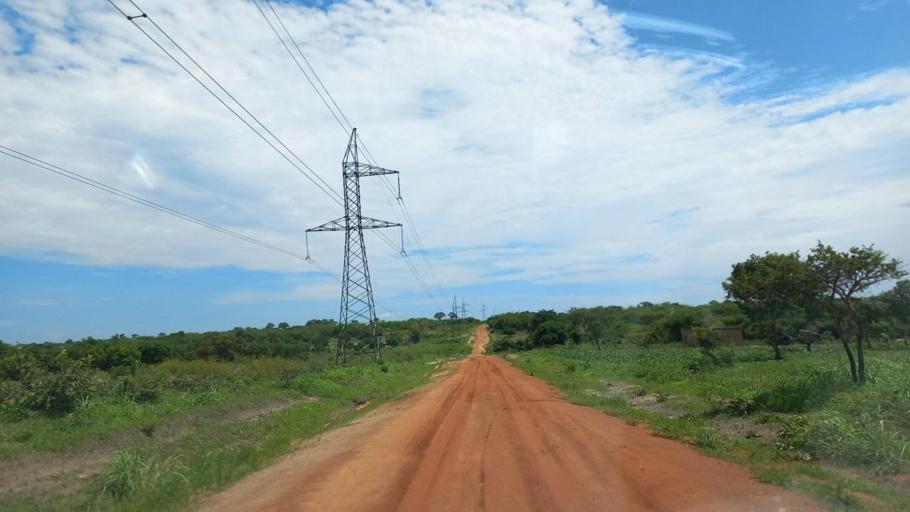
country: ZM
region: Copperbelt
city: Kitwe
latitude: -12.8310
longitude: 28.3458
